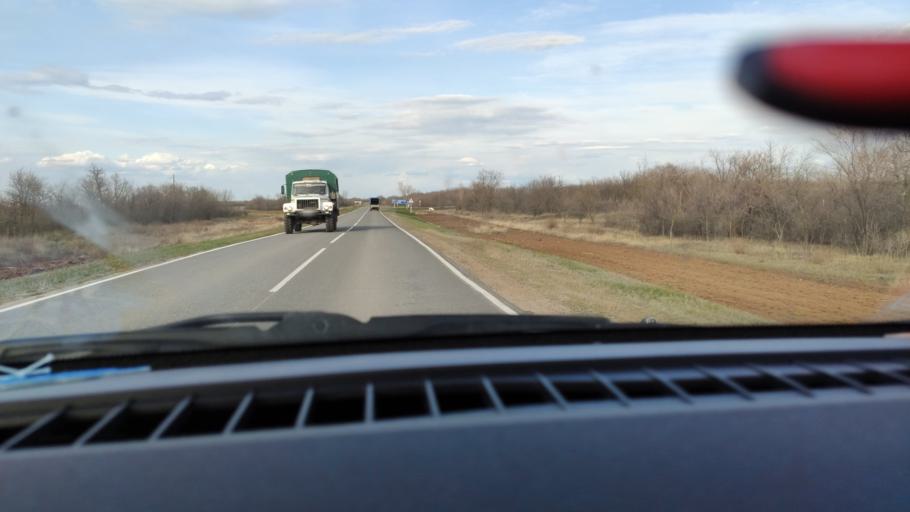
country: RU
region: Saratov
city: Privolzhskiy
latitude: 51.2839
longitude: 45.9649
